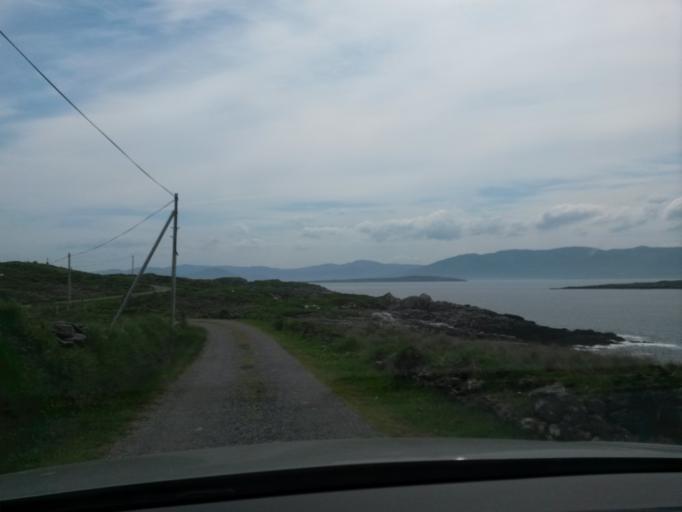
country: IE
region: Munster
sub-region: Ciarrai
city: Cahersiveen
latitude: 51.8010
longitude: -9.9458
